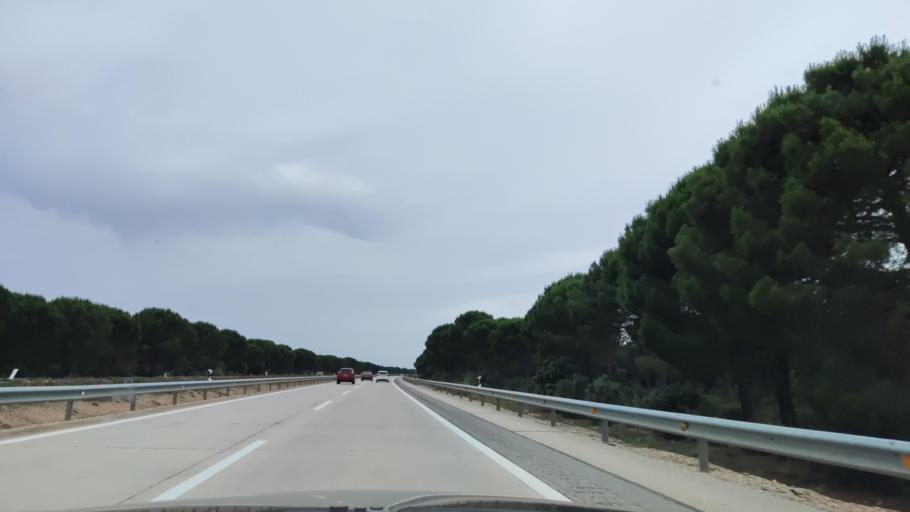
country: ES
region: Castille-La Mancha
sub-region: Provincia de Cuenca
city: Pozoamargo
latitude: 39.3407
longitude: -2.1995
